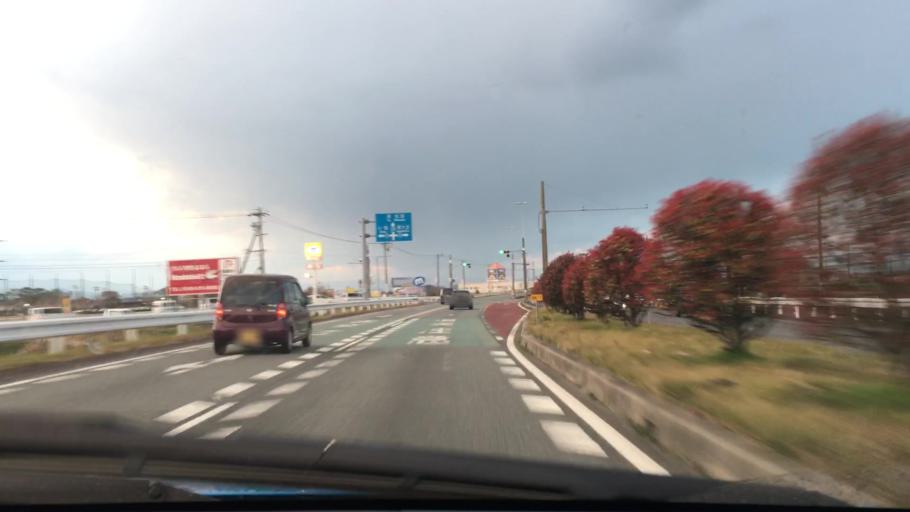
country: JP
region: Mie
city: Ise
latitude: 34.5418
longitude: 136.6641
